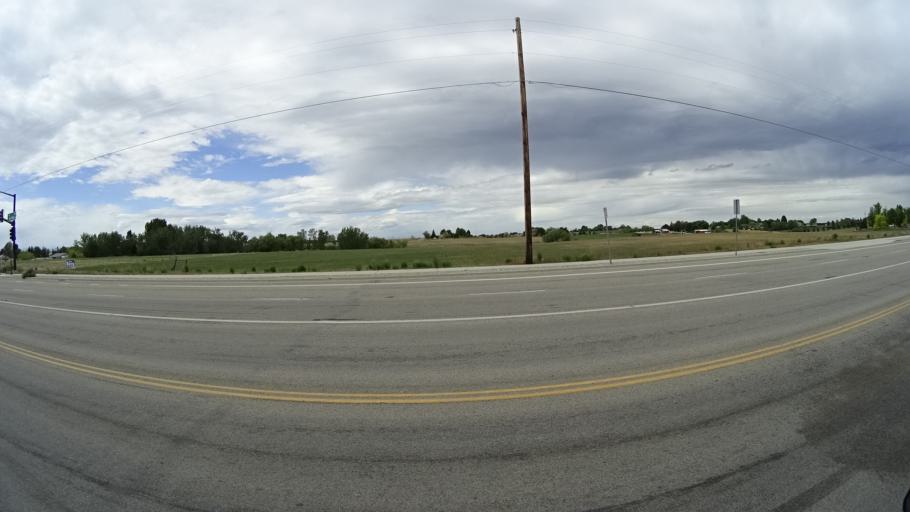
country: US
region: Idaho
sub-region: Ada County
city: Meridian
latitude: 43.5854
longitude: -116.4338
